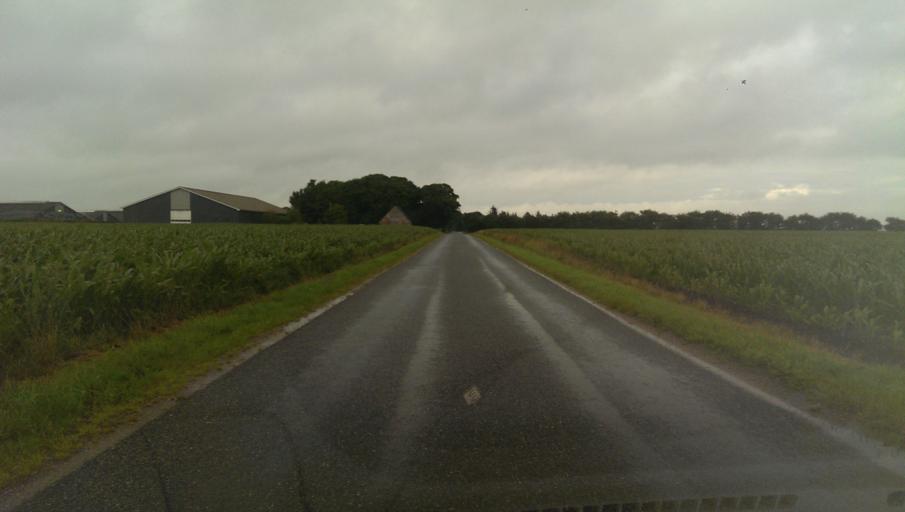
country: DK
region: South Denmark
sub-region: Esbjerg Kommune
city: Bramming
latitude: 55.4898
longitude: 8.6554
